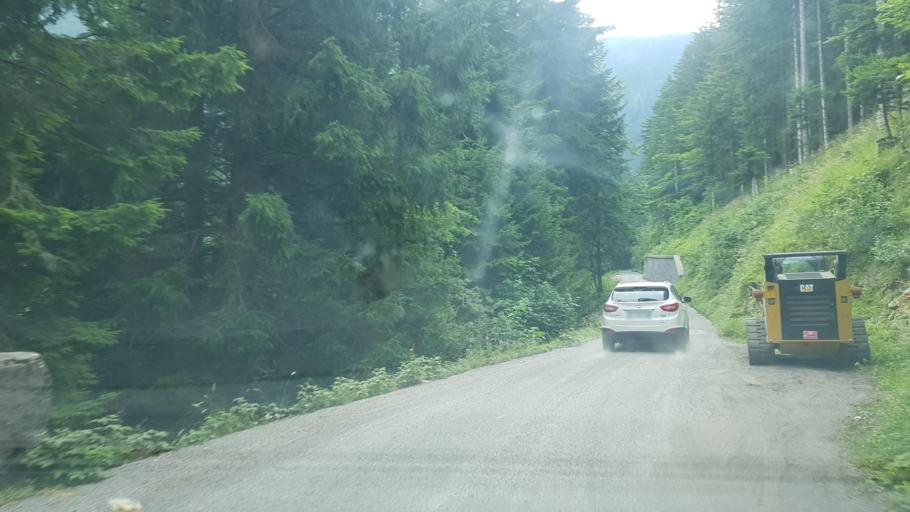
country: IT
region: Friuli Venezia Giulia
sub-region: Provincia di Udine
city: Paularo
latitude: 46.5557
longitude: 13.1205
